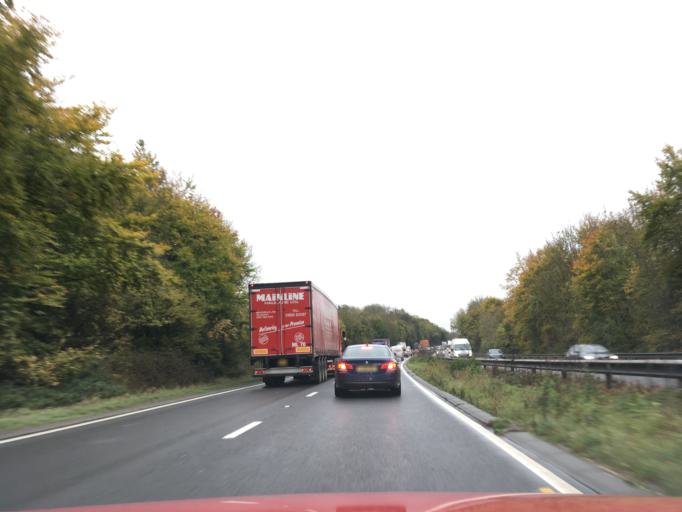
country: GB
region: England
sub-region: Hampshire
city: Kings Worthy
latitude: 51.0919
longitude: -1.3063
